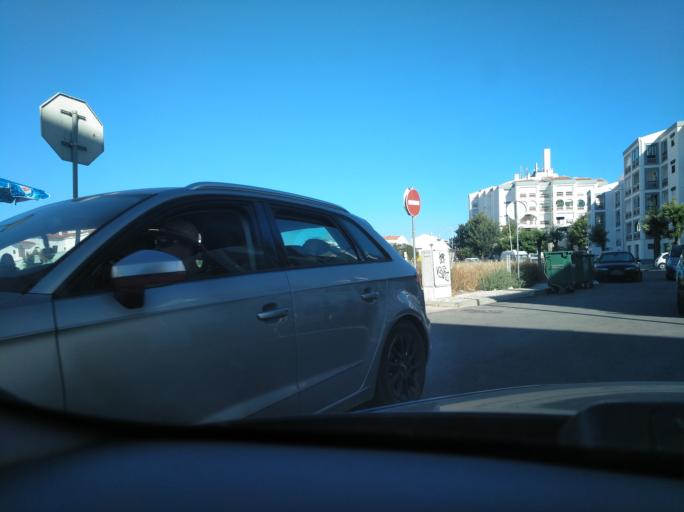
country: PT
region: Faro
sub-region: Vila Real de Santo Antonio
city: Monte Gordo
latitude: 37.1678
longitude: -7.5178
